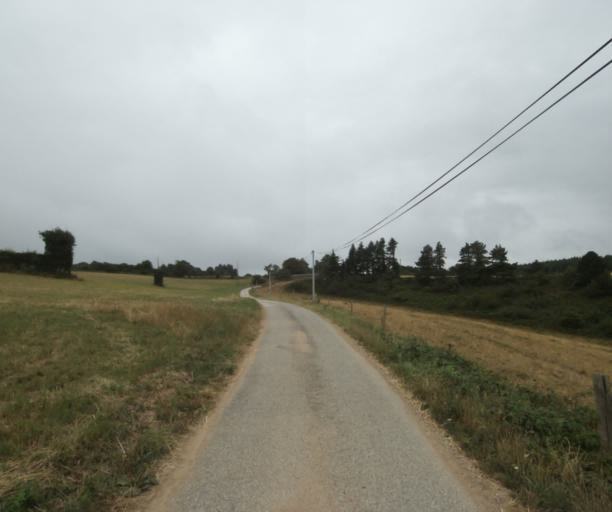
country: FR
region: Midi-Pyrenees
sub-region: Departement du Tarn
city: Soreze
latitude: 43.4132
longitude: 2.0503
